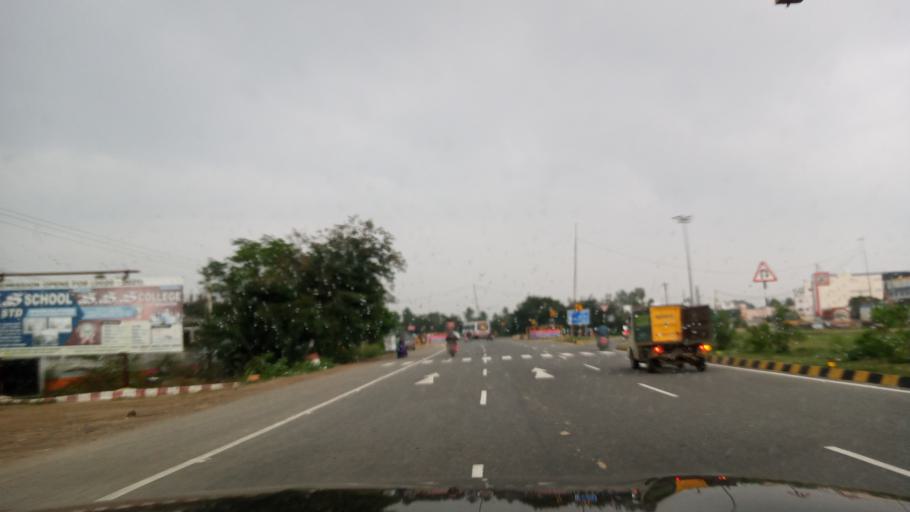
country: IN
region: Tamil Nadu
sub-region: Vellore
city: Arcot
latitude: 12.9123
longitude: 79.3216
